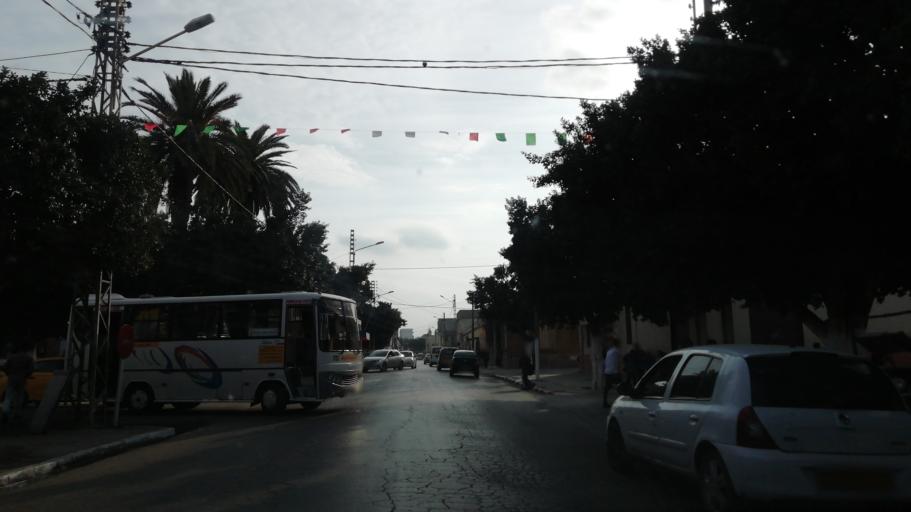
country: DZ
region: Mostaganem
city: Mostaganem
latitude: 35.8593
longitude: 0.0728
